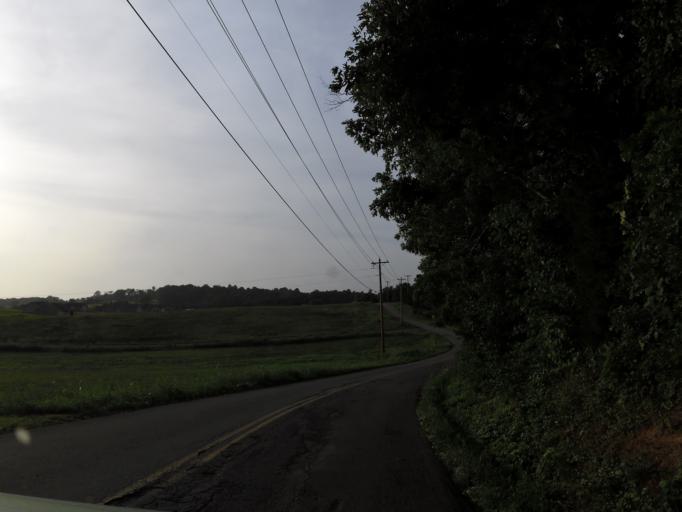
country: US
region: Tennessee
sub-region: Sevier County
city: Seymour
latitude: 35.8542
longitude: -83.7908
